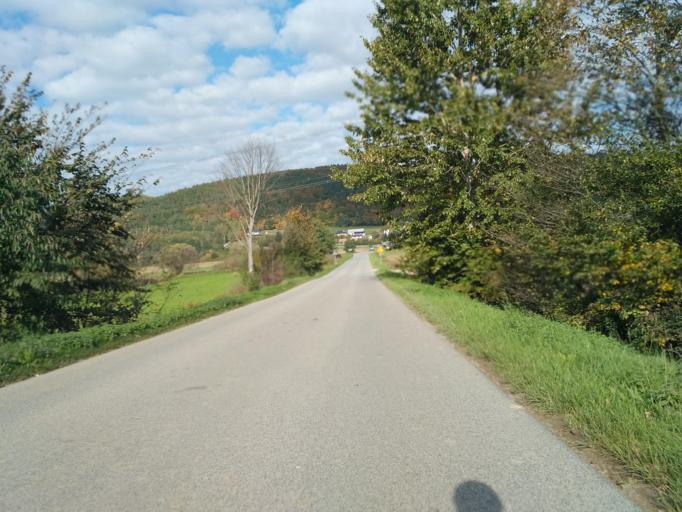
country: PL
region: Subcarpathian Voivodeship
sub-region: Powiat debicki
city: Brzostek
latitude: 49.8943
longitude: 21.3711
